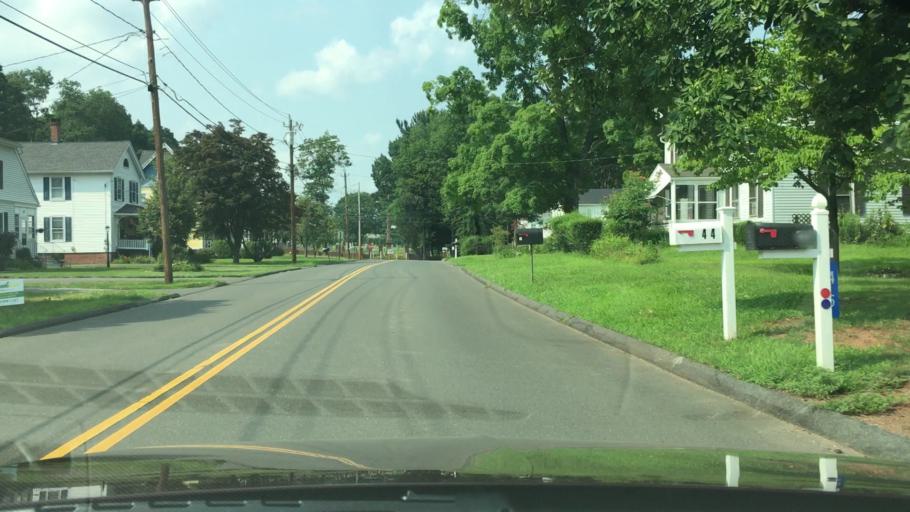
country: US
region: Connecticut
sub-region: Hartford County
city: Kensington
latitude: 41.6168
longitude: -72.7180
